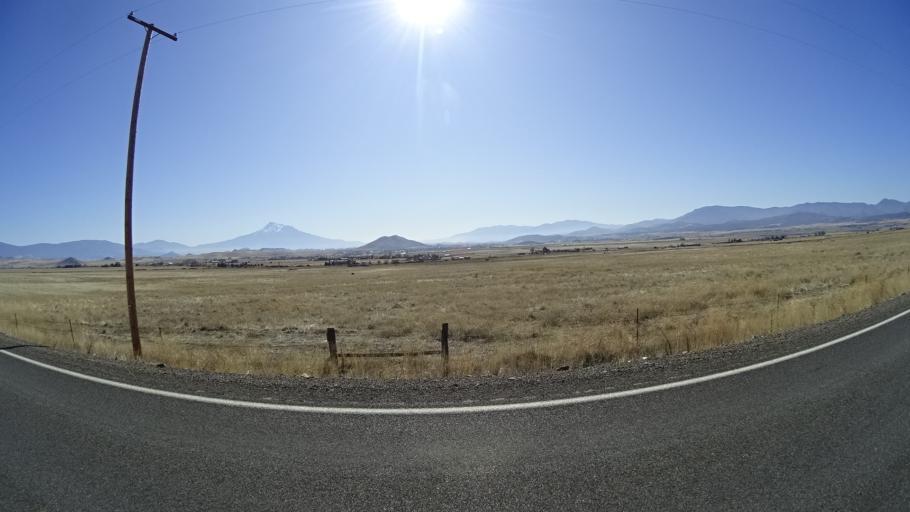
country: US
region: California
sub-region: Siskiyou County
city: Montague
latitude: 41.7707
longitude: -122.5424
